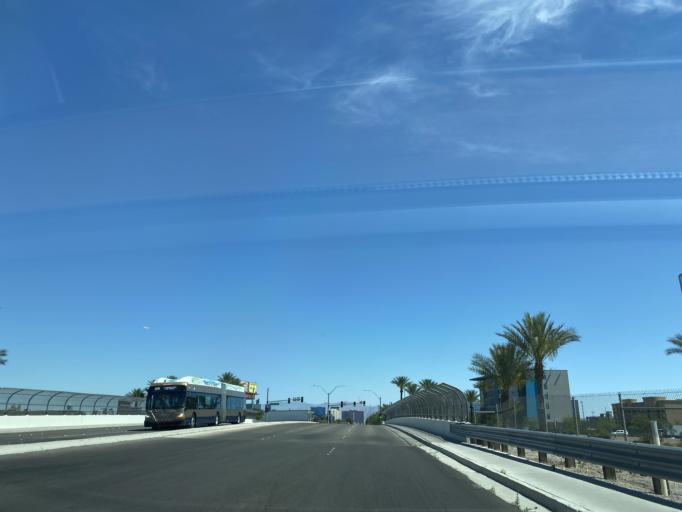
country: US
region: Nevada
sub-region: Clark County
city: Paradise
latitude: 36.0628
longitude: -115.1633
